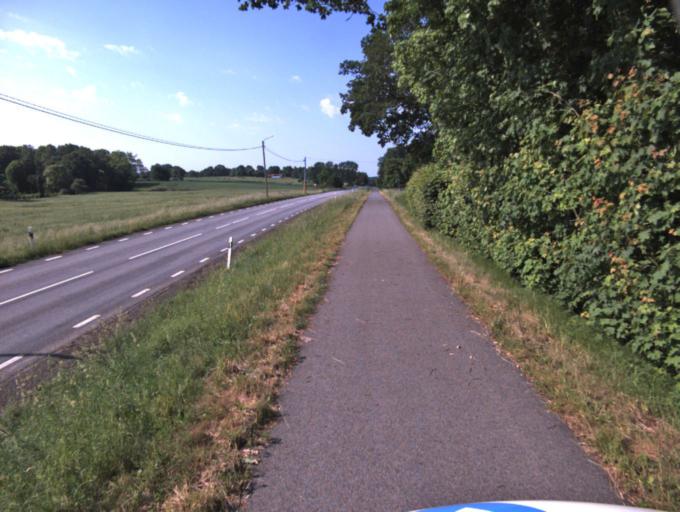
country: SE
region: Skane
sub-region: Kristianstads Kommun
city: Tollarp
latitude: 56.1665
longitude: 14.2807
